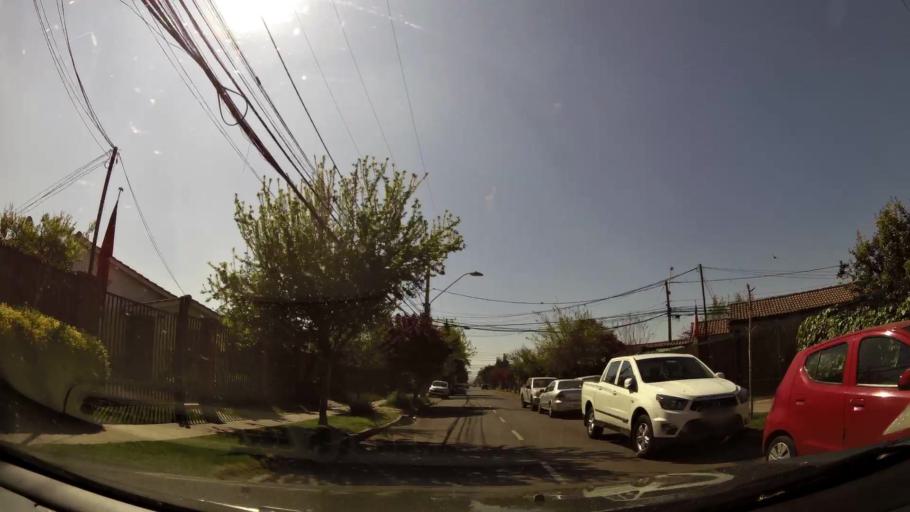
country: CL
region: Santiago Metropolitan
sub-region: Provincia de Santiago
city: Lo Prado
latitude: -33.3525
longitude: -70.7323
